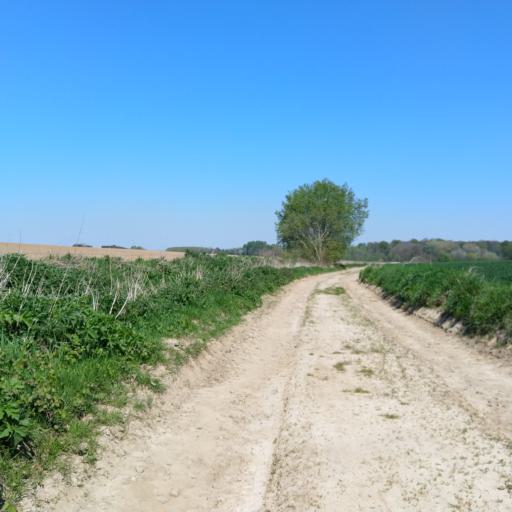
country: BE
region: Wallonia
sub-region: Province du Hainaut
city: Lens
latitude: 50.5902
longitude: 3.8990
